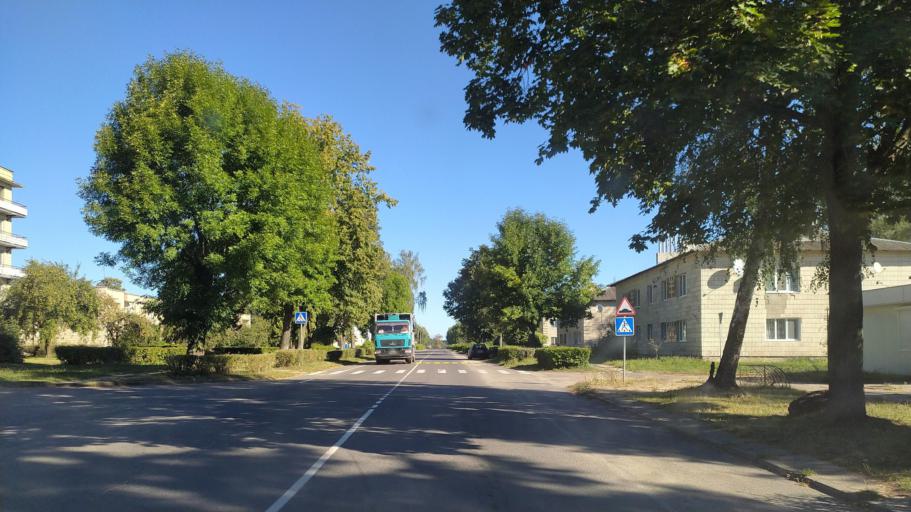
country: BY
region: Brest
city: Pruzhany
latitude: 52.4883
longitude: 24.7077
